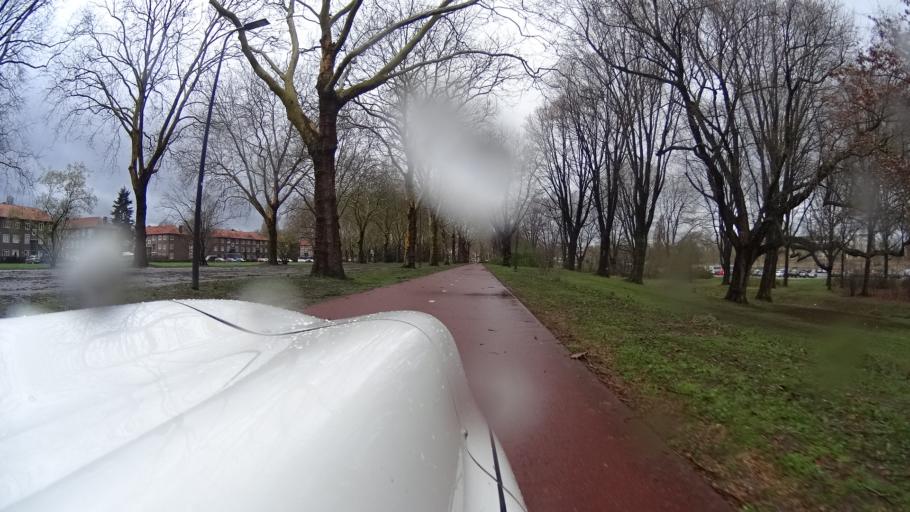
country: NL
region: North Brabant
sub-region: Gemeente 's-Hertogenbosch
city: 's-Hertogenbosch
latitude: 51.6992
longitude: 5.3247
